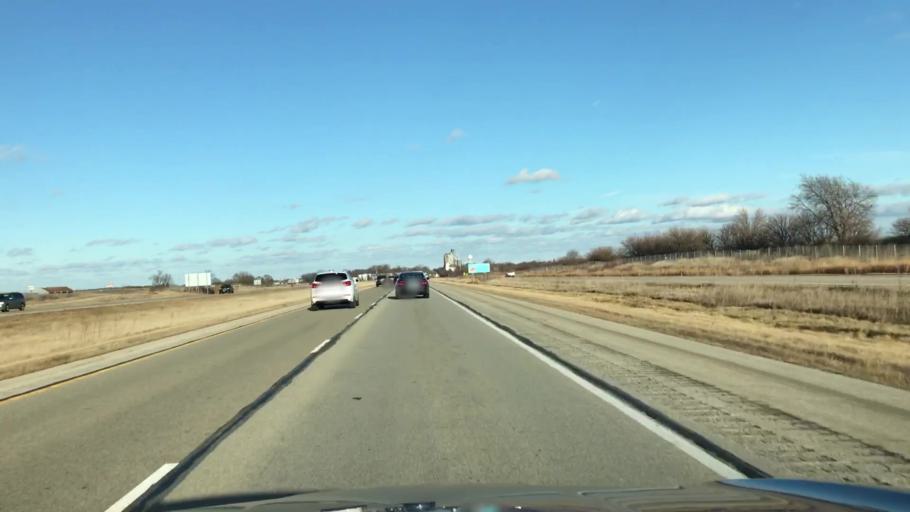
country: US
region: Illinois
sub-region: McLean County
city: Normal
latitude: 40.5535
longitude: -88.9157
